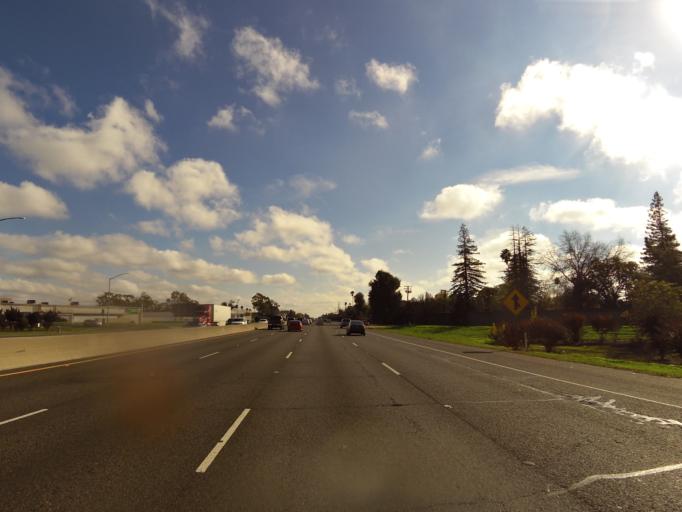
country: US
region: California
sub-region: Sacramento County
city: Parkway
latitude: 38.4956
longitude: -121.4457
